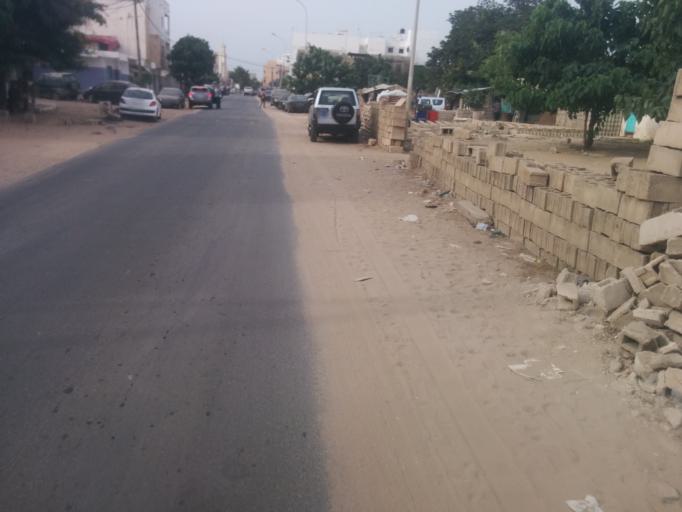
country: SN
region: Dakar
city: Grand Dakar
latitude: 14.7319
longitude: -17.4573
